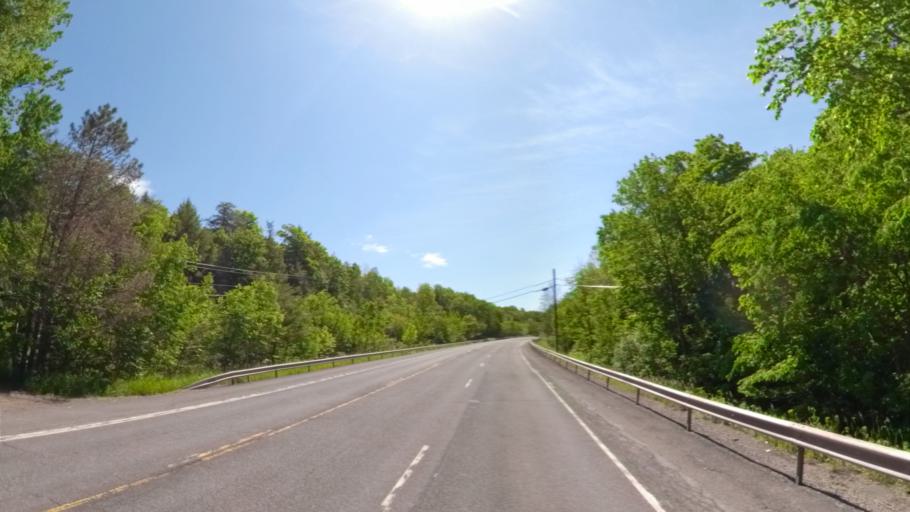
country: US
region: New York
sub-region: Delaware County
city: Stamford
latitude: 42.1496
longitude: -74.4988
